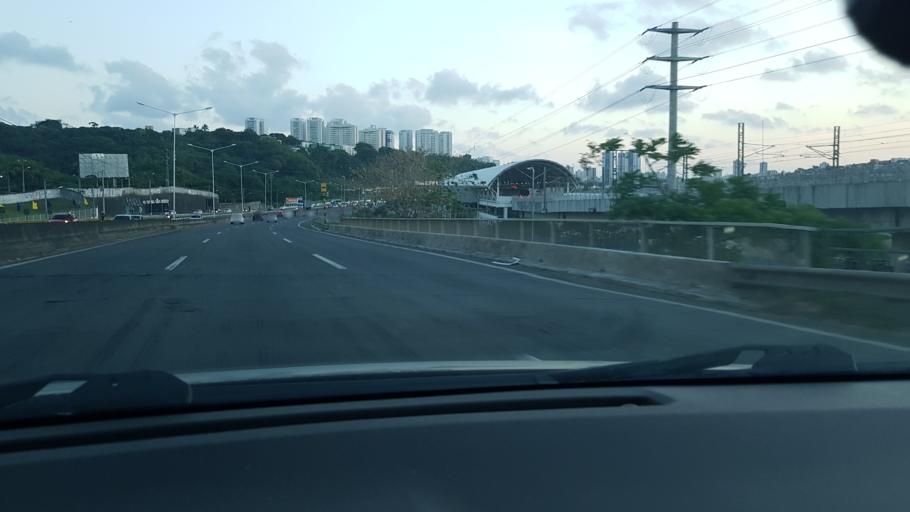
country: BR
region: Bahia
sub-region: Salvador
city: Salvador
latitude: -12.9539
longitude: -38.4713
